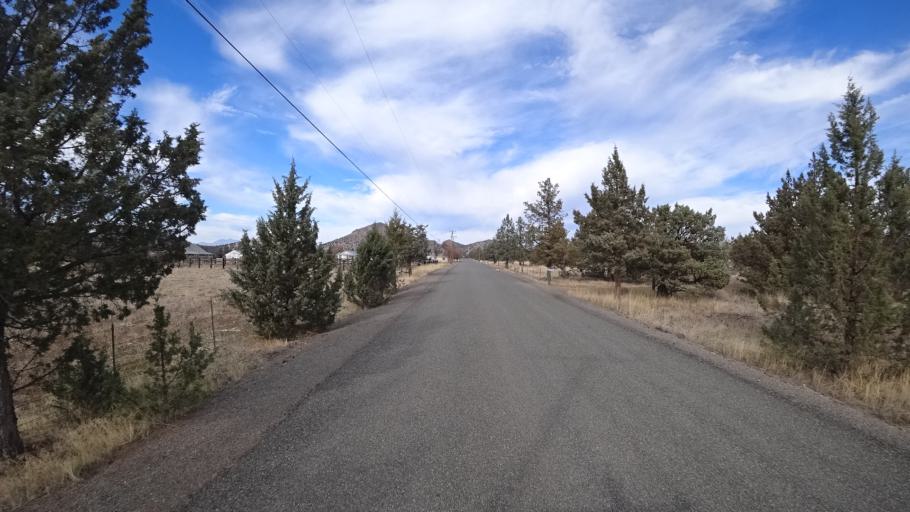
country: US
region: California
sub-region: Siskiyou County
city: Montague
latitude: 41.6422
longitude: -122.4189
